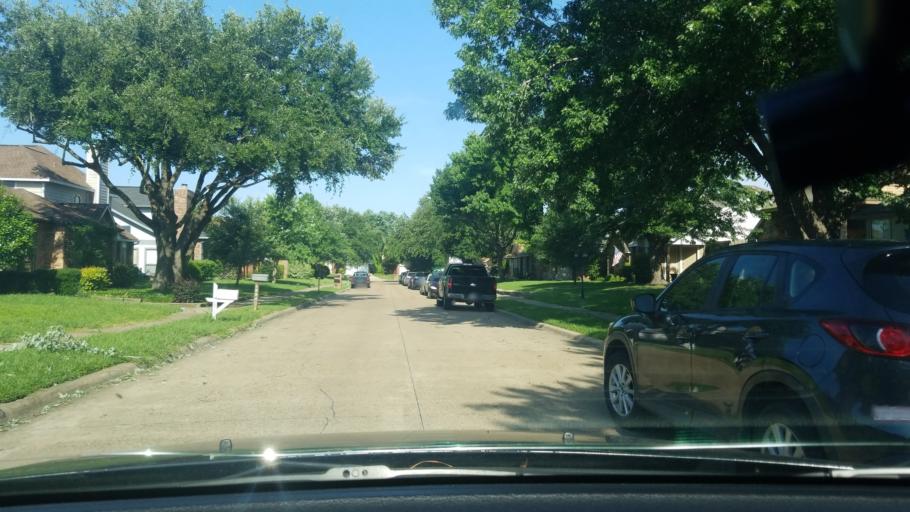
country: US
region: Texas
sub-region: Dallas County
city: Sunnyvale
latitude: 32.7785
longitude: -96.5770
